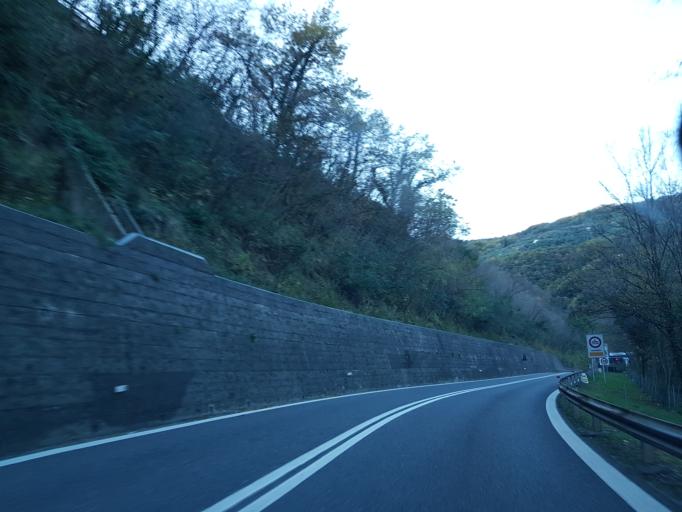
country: IT
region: Liguria
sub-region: Provincia di Genova
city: Avegno
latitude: 44.3755
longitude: 9.1486
